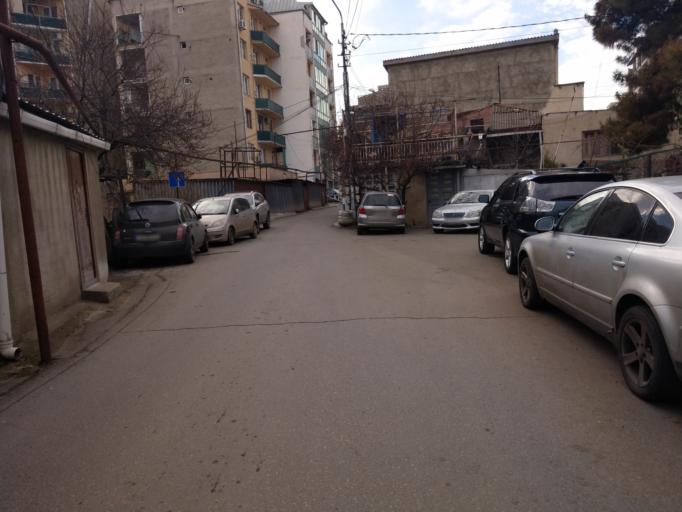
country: GE
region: T'bilisi
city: Tbilisi
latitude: 41.7227
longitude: 44.7665
